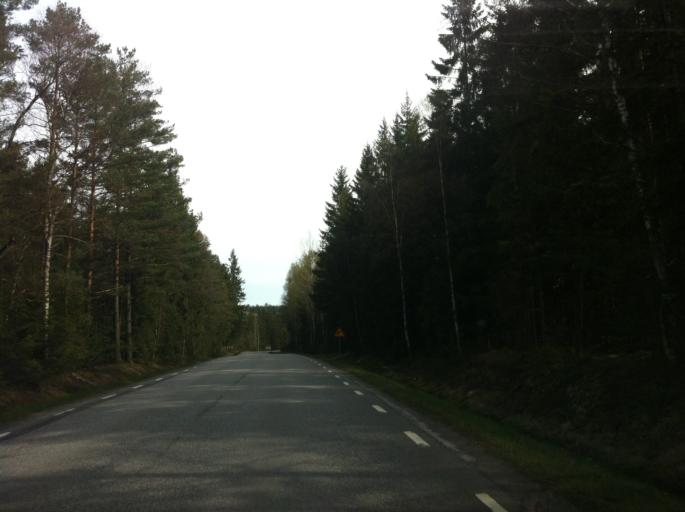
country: SE
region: Vaestra Goetaland
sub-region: Marks Kommun
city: Fritsla
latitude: 57.3986
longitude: 12.8161
